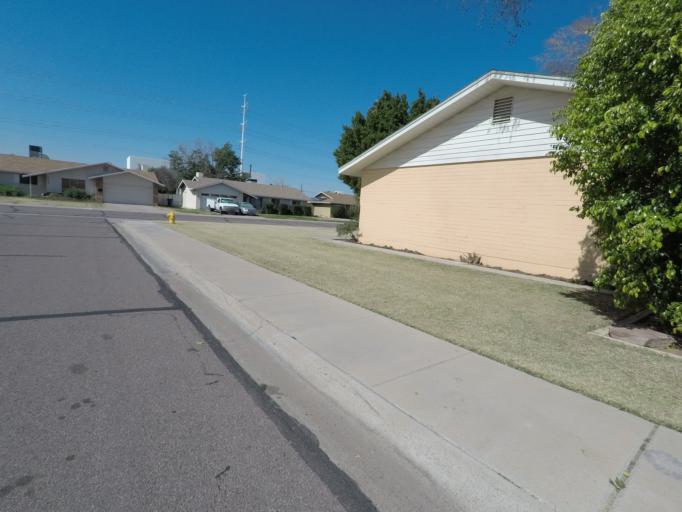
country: US
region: Arizona
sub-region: Maricopa County
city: Tempe Junction
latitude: 33.3959
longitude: -111.9423
